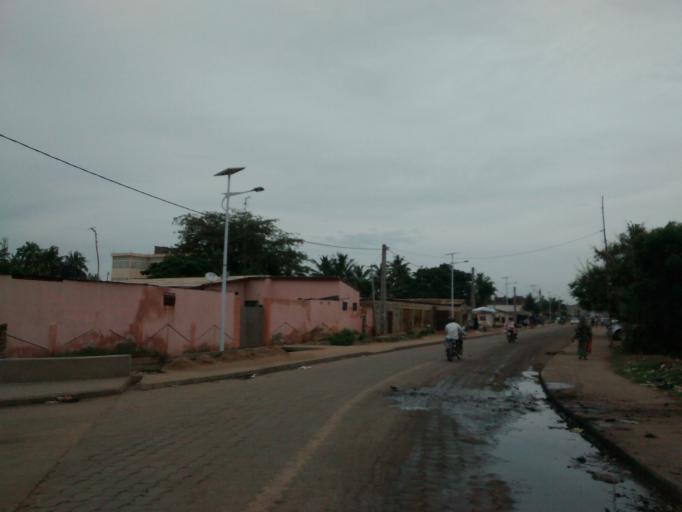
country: TG
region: Maritime
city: Lome
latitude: 6.1540
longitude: 1.2104
